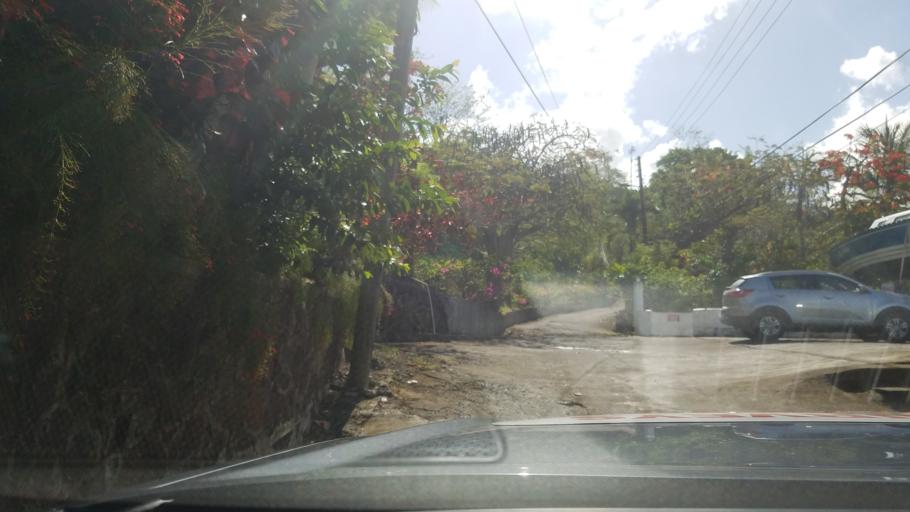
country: LC
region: Castries Quarter
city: Castries
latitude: 14.0217
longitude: -61.0041
